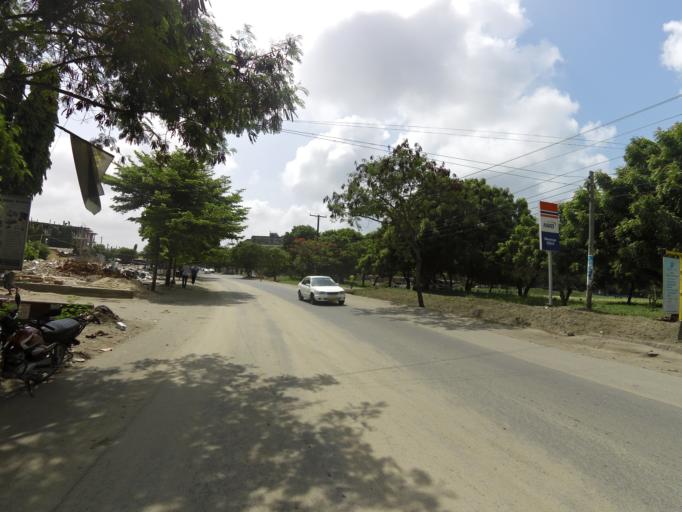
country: TZ
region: Dar es Salaam
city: Magomeni
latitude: -6.7684
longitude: 39.2285
